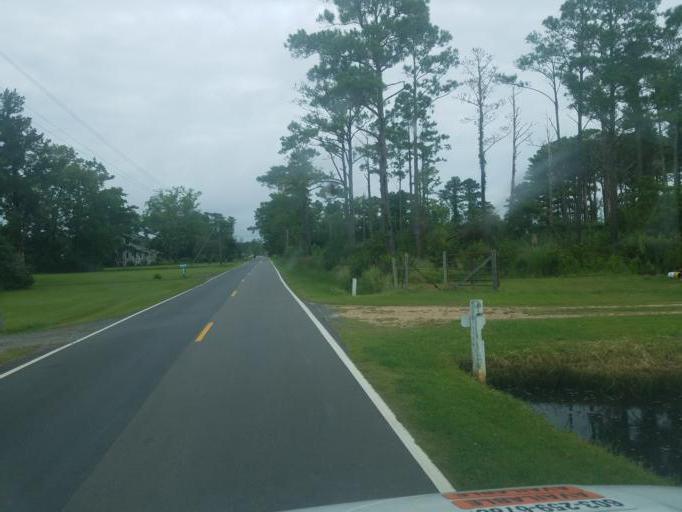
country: US
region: North Carolina
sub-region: Dare County
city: Manteo
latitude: 35.8818
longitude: -75.7602
